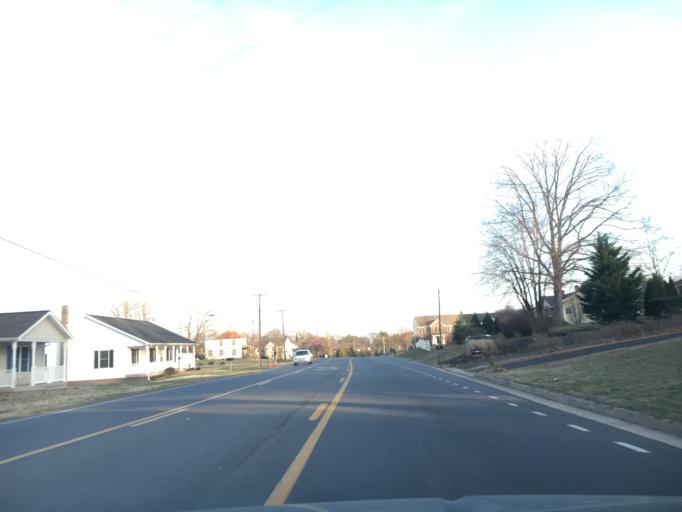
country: US
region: Virginia
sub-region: Culpeper County
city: Culpeper
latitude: 38.4829
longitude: -78.0135
